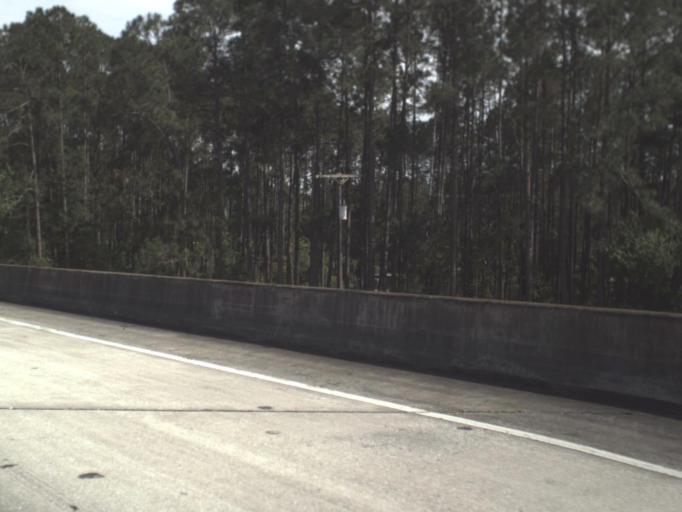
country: US
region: Florida
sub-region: Baker County
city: Macclenny
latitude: 30.2390
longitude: -82.3042
